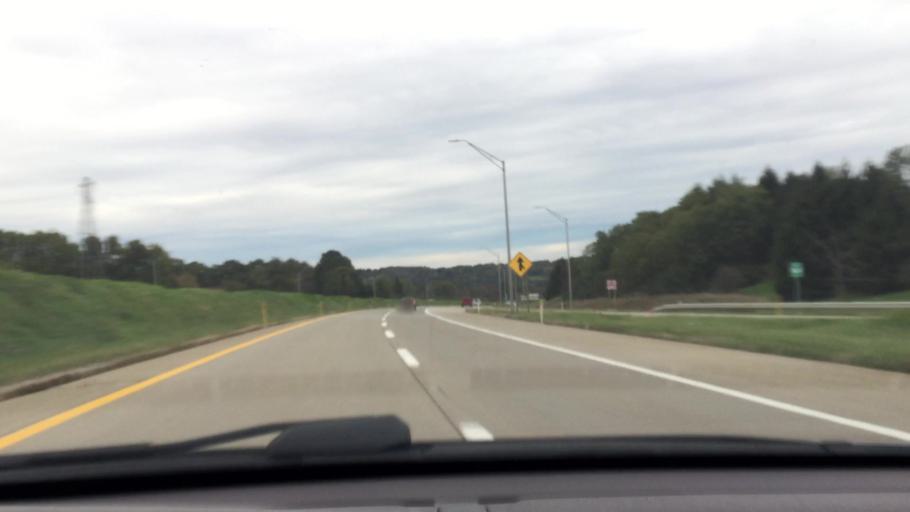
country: US
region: Pennsylvania
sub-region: Lawrence County
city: Oakland
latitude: 40.9743
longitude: -80.4004
